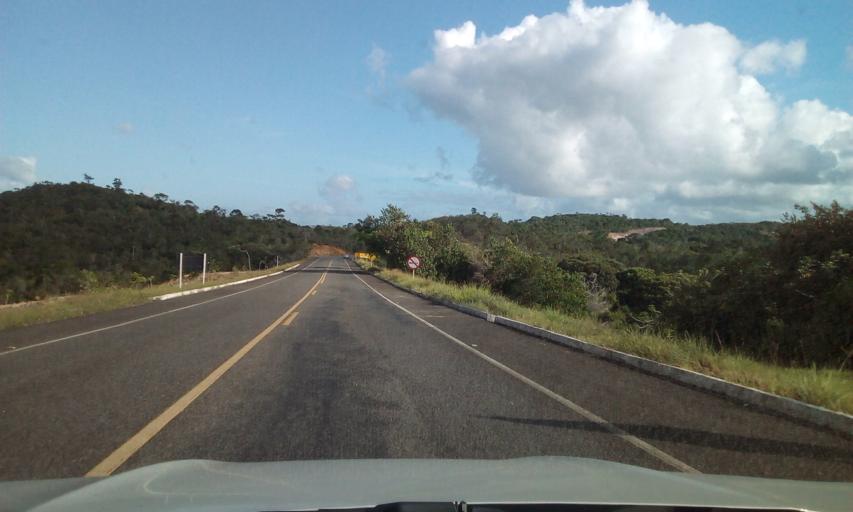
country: BR
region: Bahia
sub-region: Conde
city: Conde
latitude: -12.0928
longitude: -37.7732
